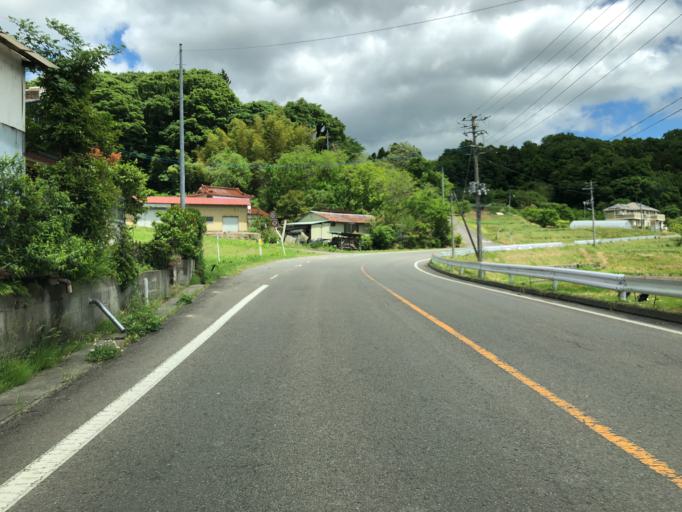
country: JP
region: Fukushima
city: Motomiya
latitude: 37.5181
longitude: 140.4500
